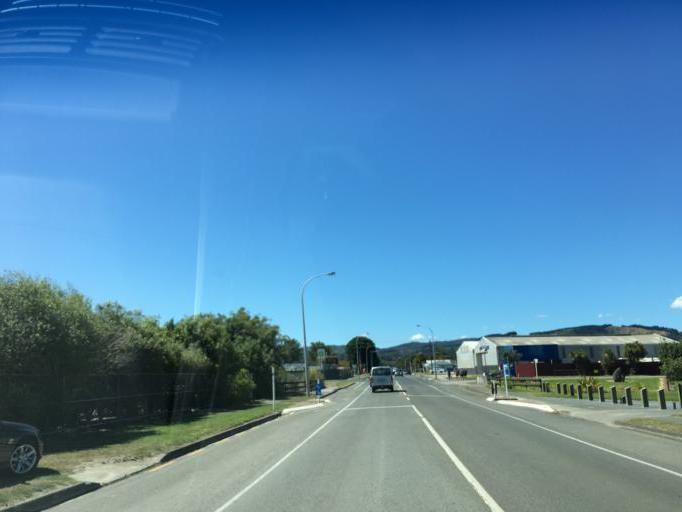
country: NZ
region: Gisborne
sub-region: Gisborne District
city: Gisborne
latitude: -38.6656
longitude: 178.0054
